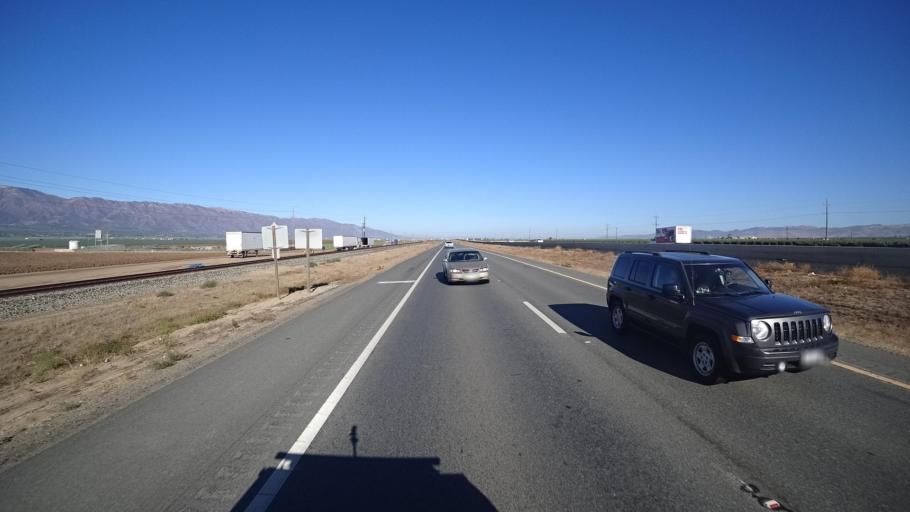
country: US
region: California
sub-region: Monterey County
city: Gonzales
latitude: 36.4682
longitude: -121.3963
